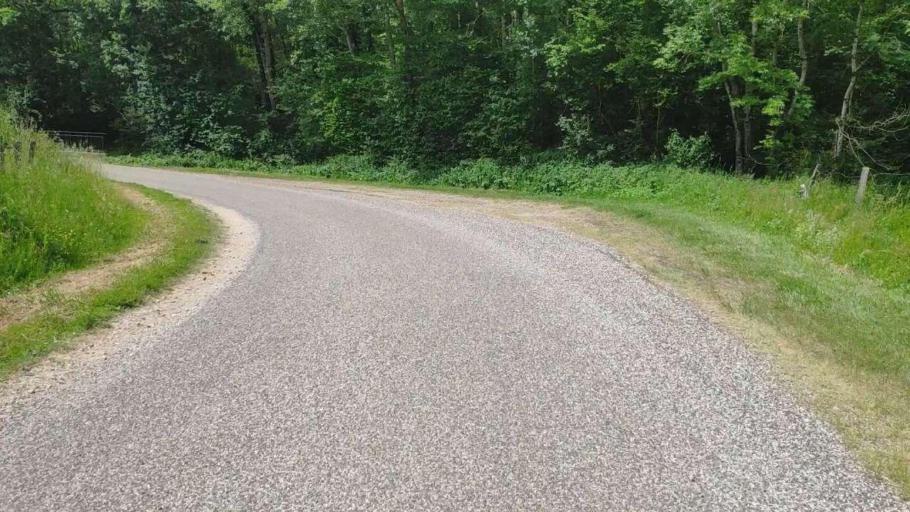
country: FR
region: Franche-Comte
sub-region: Departement du Jura
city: Montmorot
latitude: 46.7434
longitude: 5.5345
